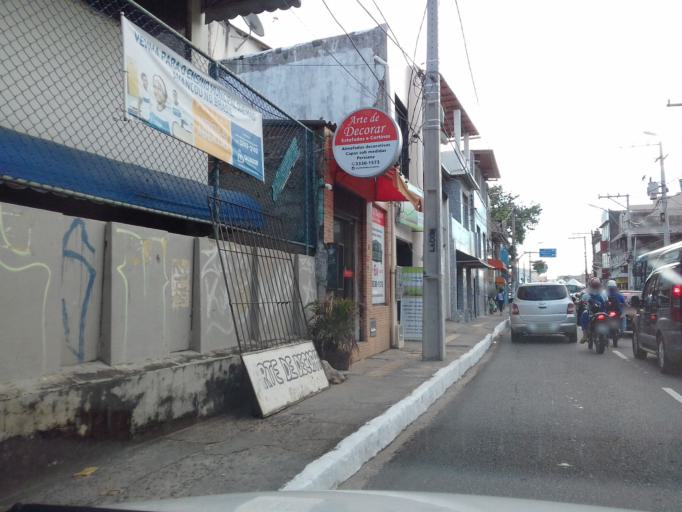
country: BR
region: Bahia
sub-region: Salvador
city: Salvador
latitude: -13.0129
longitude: -38.4876
